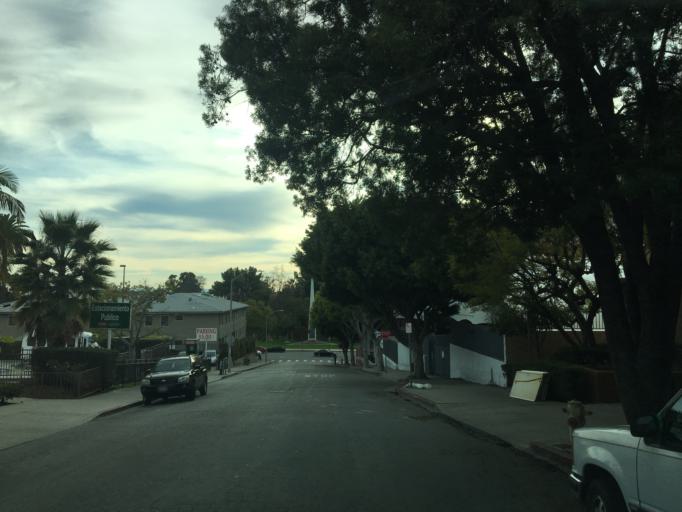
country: US
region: California
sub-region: Los Angeles County
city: Echo Park
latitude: 34.0619
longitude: -118.2774
